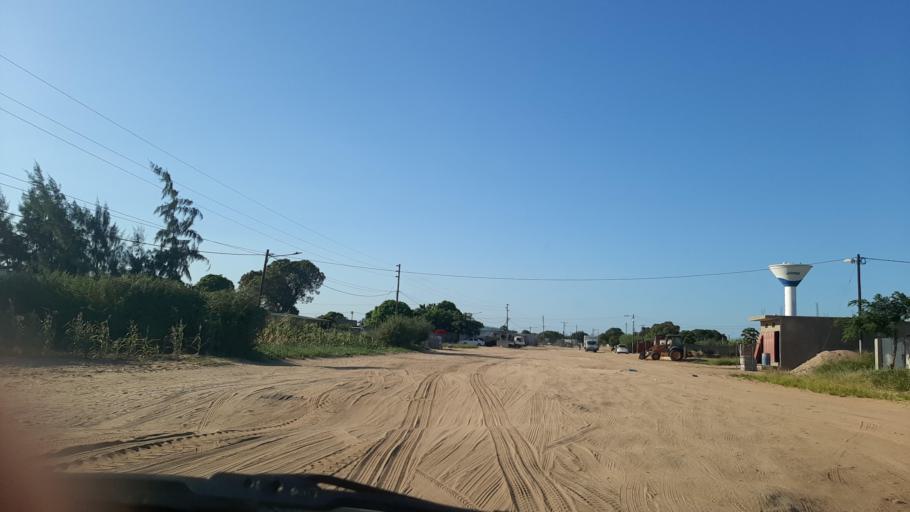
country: MZ
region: Maputo City
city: Maputo
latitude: -25.7901
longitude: 32.5522
